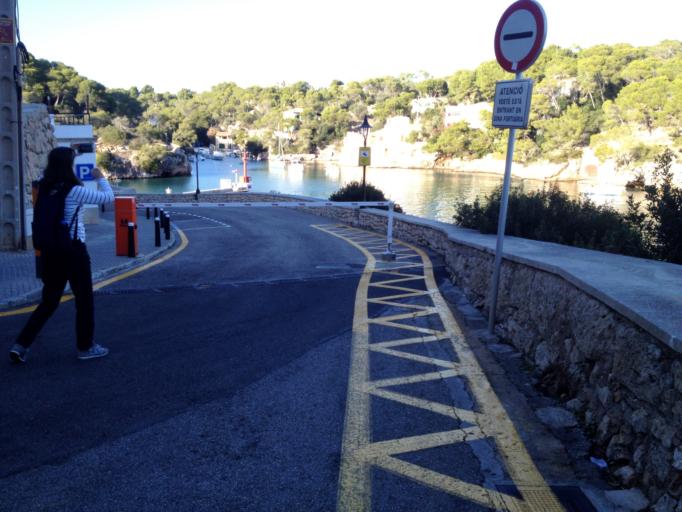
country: ES
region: Balearic Islands
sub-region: Illes Balears
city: Santanyi
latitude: 39.3309
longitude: 3.1706
